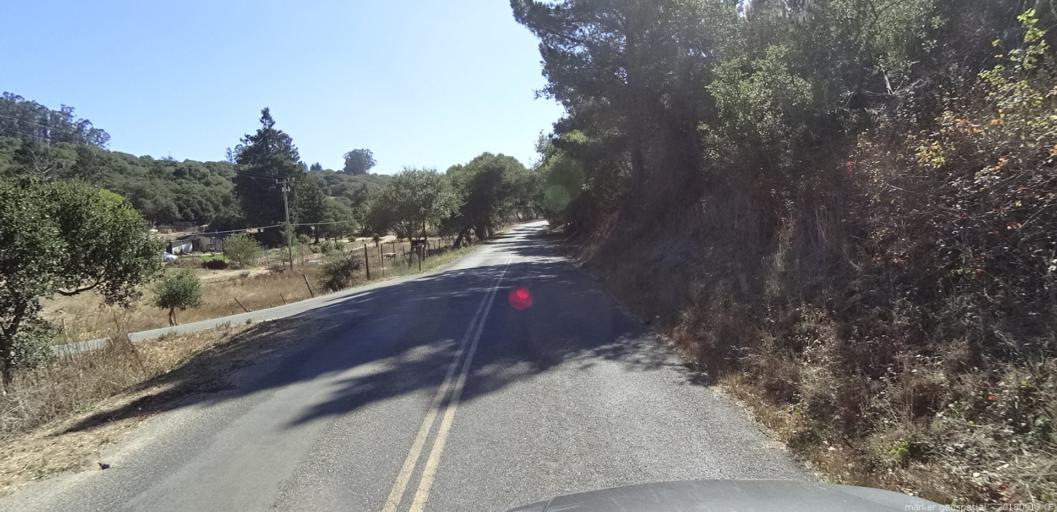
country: US
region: California
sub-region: Monterey County
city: Elkhorn
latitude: 36.8389
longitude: -121.7124
